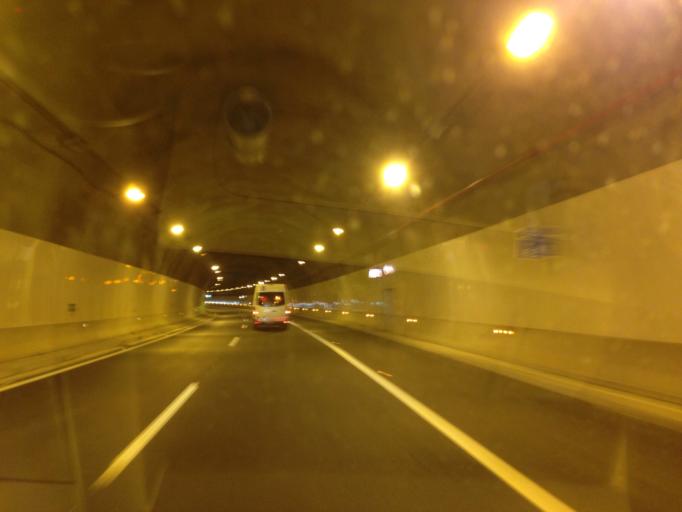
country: ES
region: Canary Islands
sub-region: Provincia de Las Palmas
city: Puerto Rico
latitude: 27.8037
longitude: -15.7078
